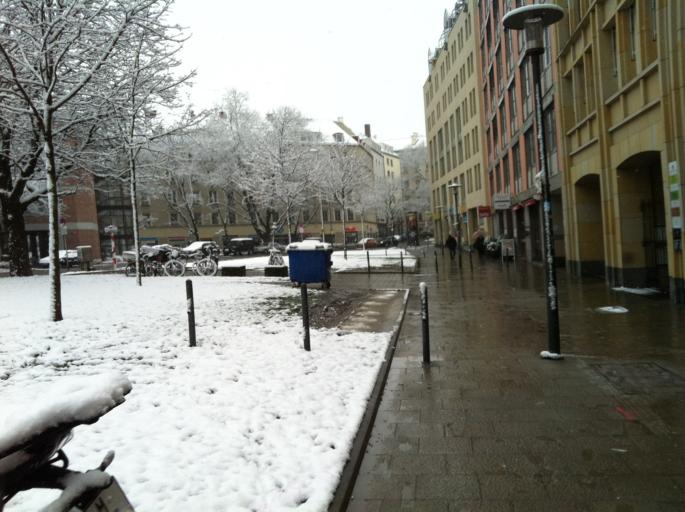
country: DE
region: Bavaria
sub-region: Upper Bavaria
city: Munich
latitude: 48.1340
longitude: 11.5701
